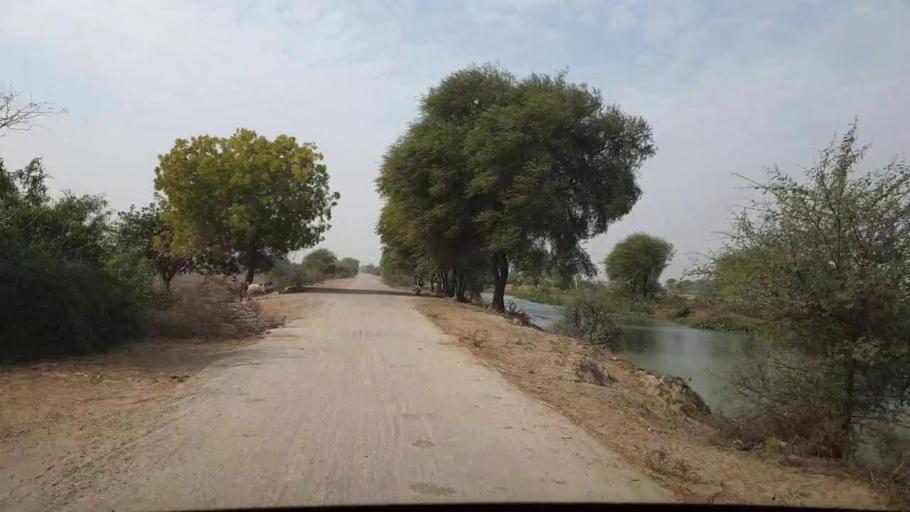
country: PK
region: Sindh
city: Chuhar Jamali
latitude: 24.3878
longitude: 67.9455
